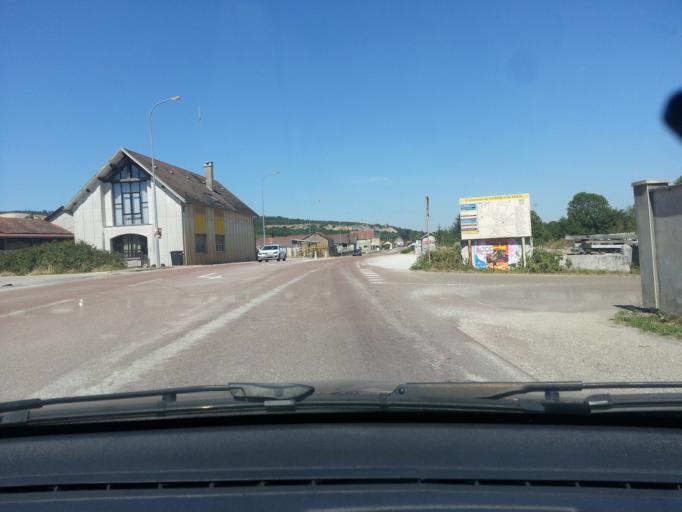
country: FR
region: Bourgogne
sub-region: Departement de la Cote-d'Or
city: Nuits-Saint-Georges
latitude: 47.0984
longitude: 4.9138
